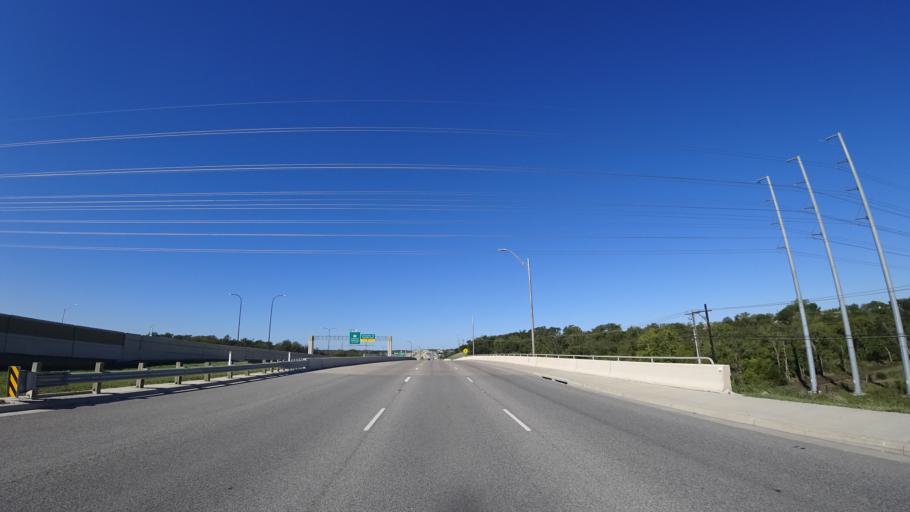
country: US
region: Texas
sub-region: Travis County
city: Manor
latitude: 30.3298
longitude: -97.6432
